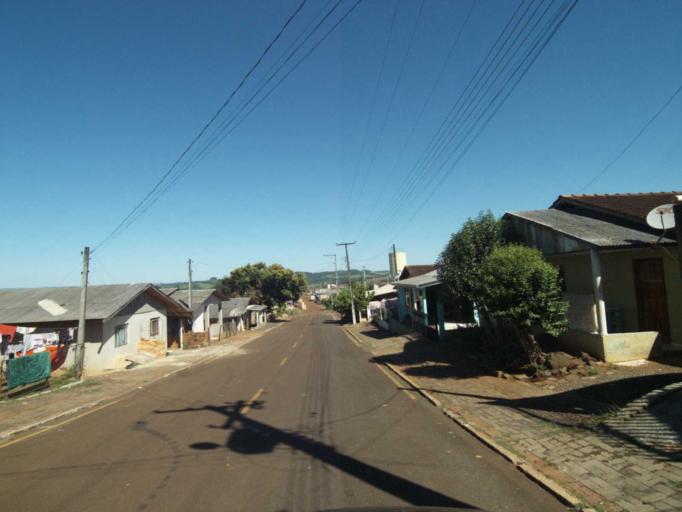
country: BR
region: Parana
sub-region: Coronel Vivida
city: Coronel Vivida
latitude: -25.9586
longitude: -52.8097
